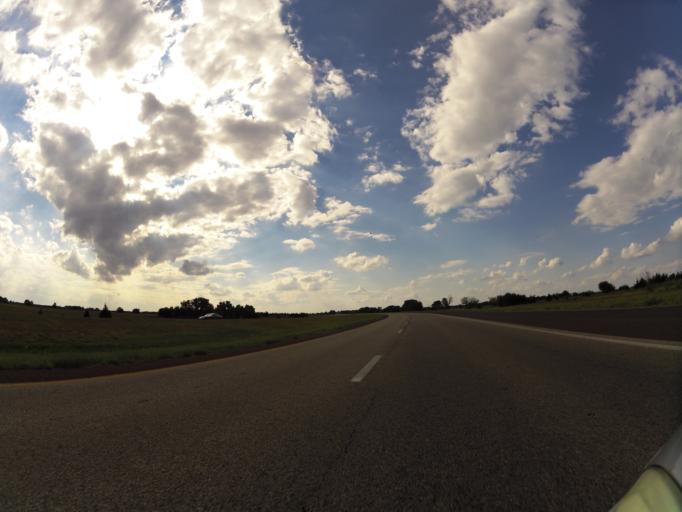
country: US
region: Kansas
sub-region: Reno County
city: South Hutchinson
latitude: 37.9467
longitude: -97.8863
